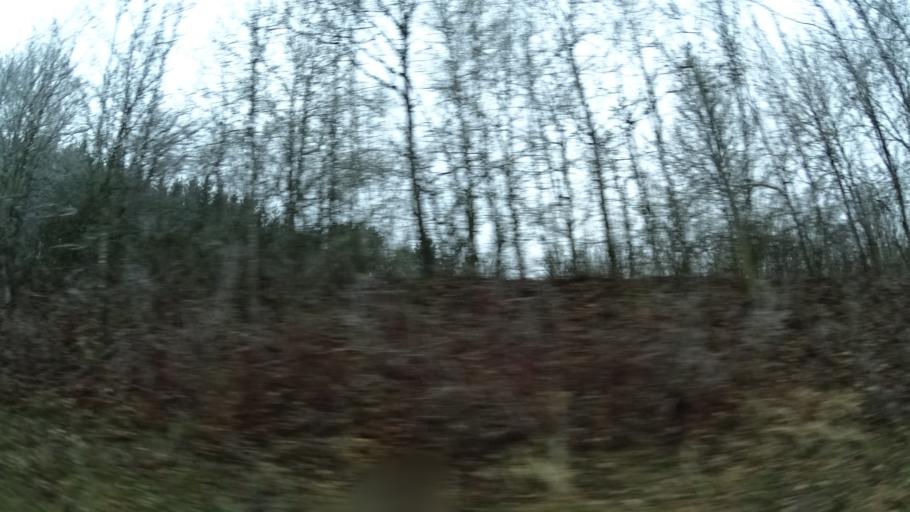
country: DE
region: Baden-Wuerttemberg
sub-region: Regierungsbezirk Stuttgart
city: Boxberg
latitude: 49.4765
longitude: 9.6271
